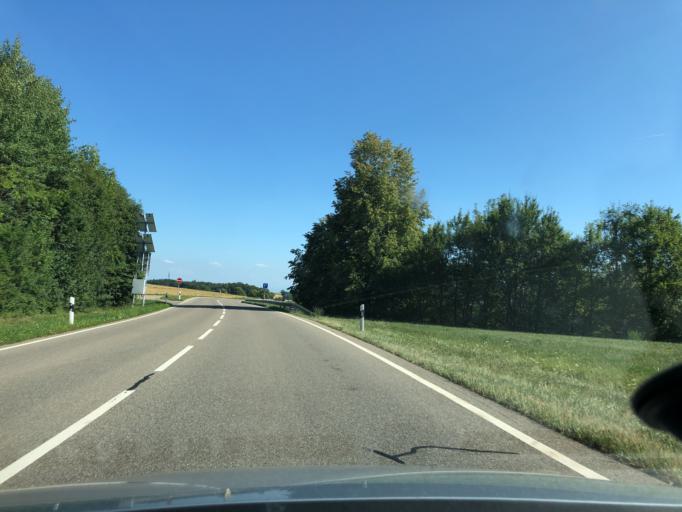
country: DE
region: Baden-Wuerttemberg
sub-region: Freiburg Region
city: Dogern
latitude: 47.6685
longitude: 8.1570
